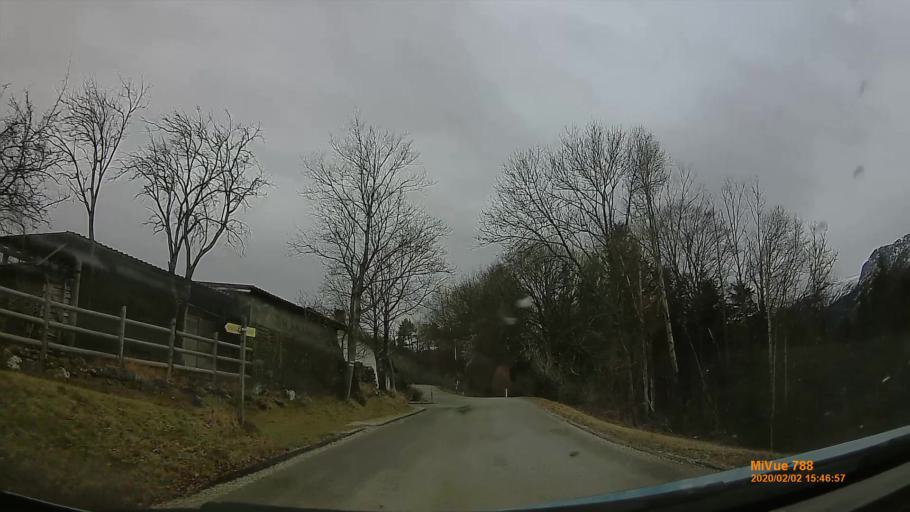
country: AT
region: Lower Austria
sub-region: Politischer Bezirk Neunkirchen
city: Reichenau an der Rax
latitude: 47.6921
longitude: 15.8185
